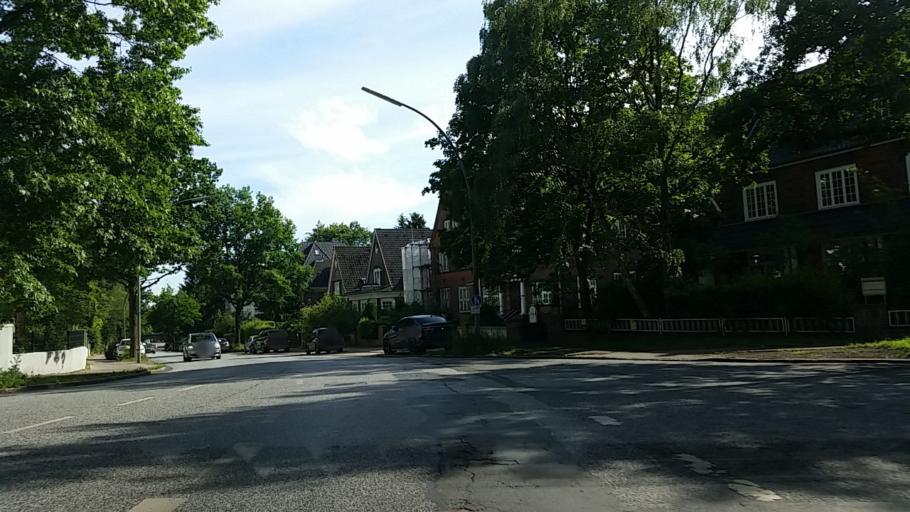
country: DE
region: Hamburg
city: Altona
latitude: 53.5624
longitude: 9.8869
